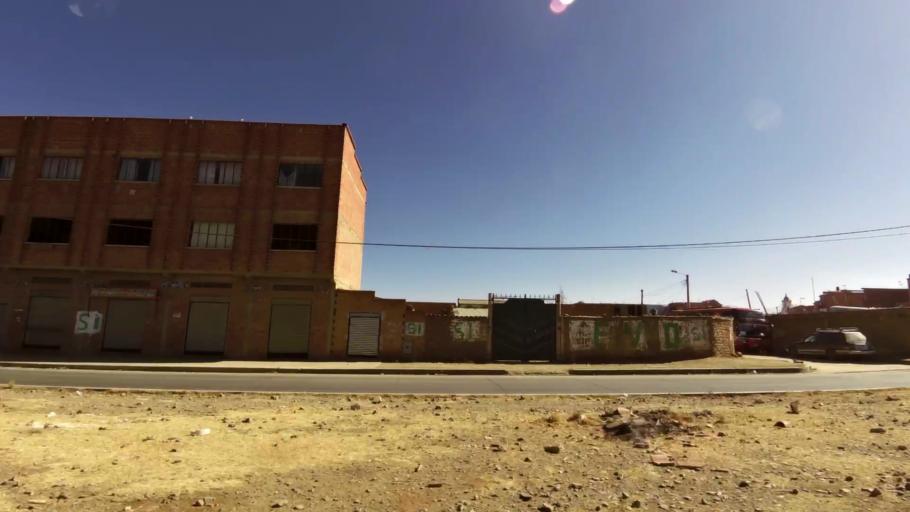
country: BO
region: La Paz
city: La Paz
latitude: -16.5301
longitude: -68.2096
